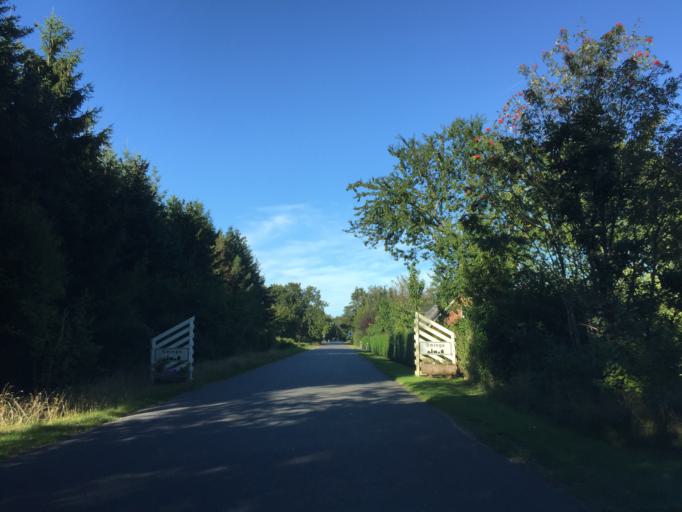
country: DK
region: Central Jutland
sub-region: Silkeborg Kommune
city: Svejbaek
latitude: 56.2106
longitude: 9.6798
